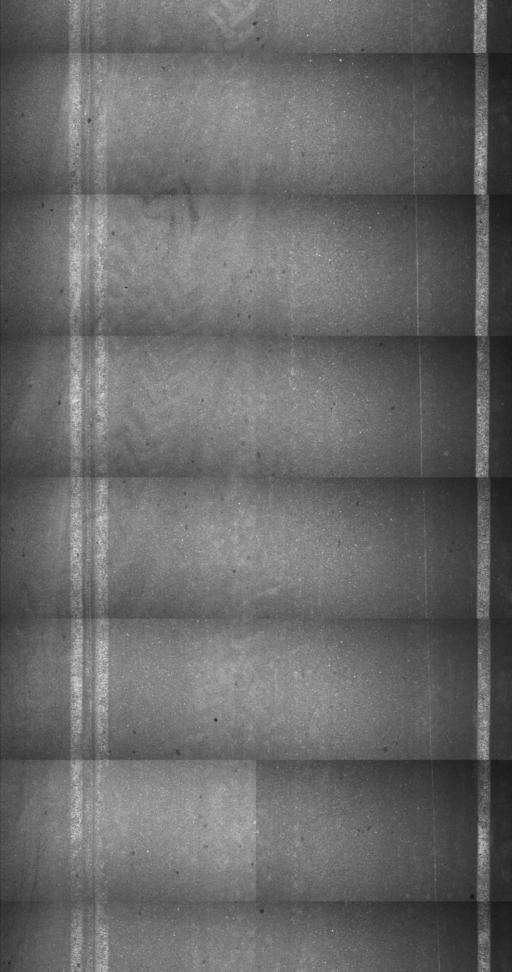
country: US
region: New Hampshire
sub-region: Coos County
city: Colebrook
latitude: 44.9577
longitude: -71.5264
